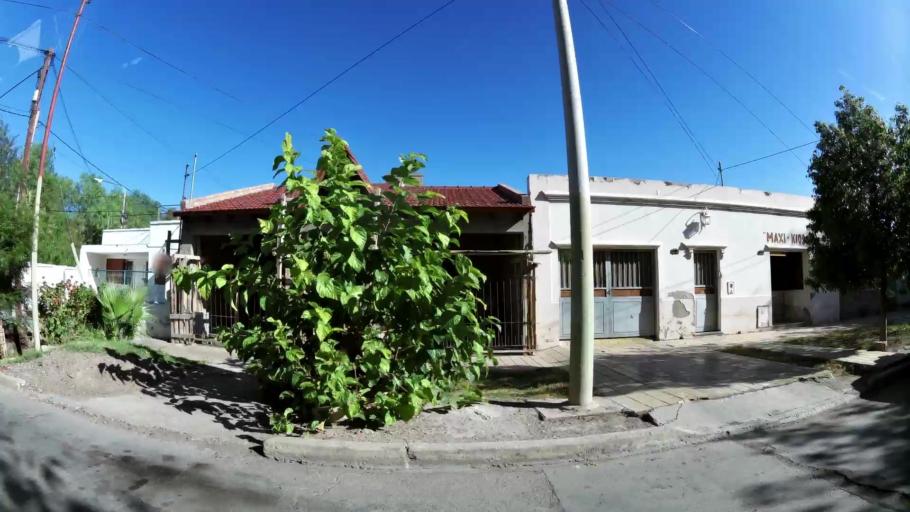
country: AR
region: San Juan
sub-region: Departamento de Santa Lucia
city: Santa Lucia
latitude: -31.5345
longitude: -68.5122
